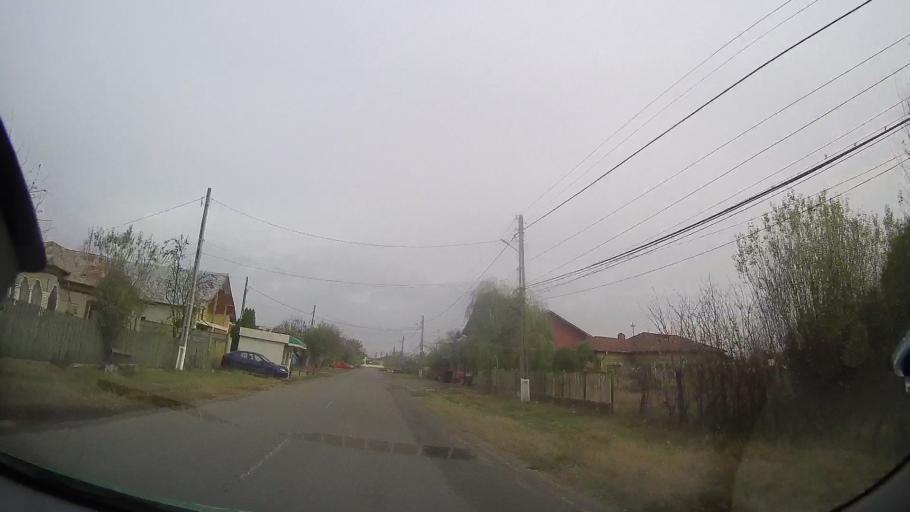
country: RO
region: Prahova
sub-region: Comuna Balta Doamnei
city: Balta Doamnei
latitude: 44.7590
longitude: 26.1650
